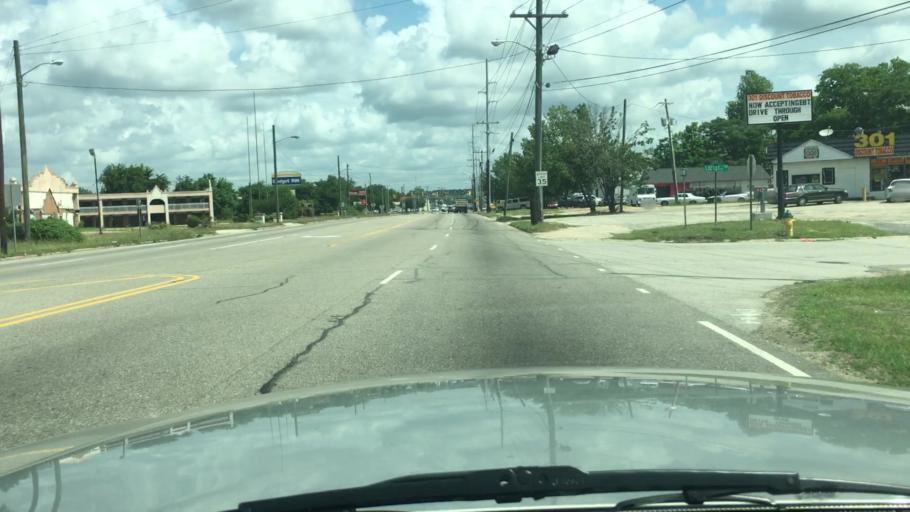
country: US
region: North Carolina
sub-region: Cumberland County
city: Fayetteville
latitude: 35.0434
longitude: -78.8659
